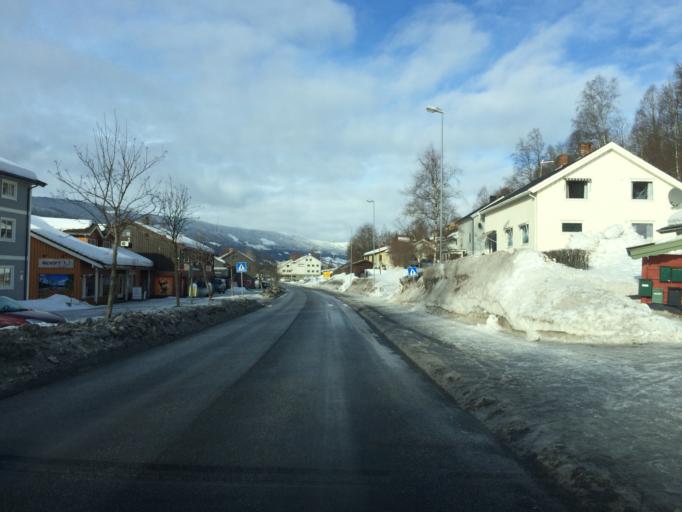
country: NO
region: Oppland
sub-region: Gausdal
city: Segalstad bru
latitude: 61.2272
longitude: 10.2257
